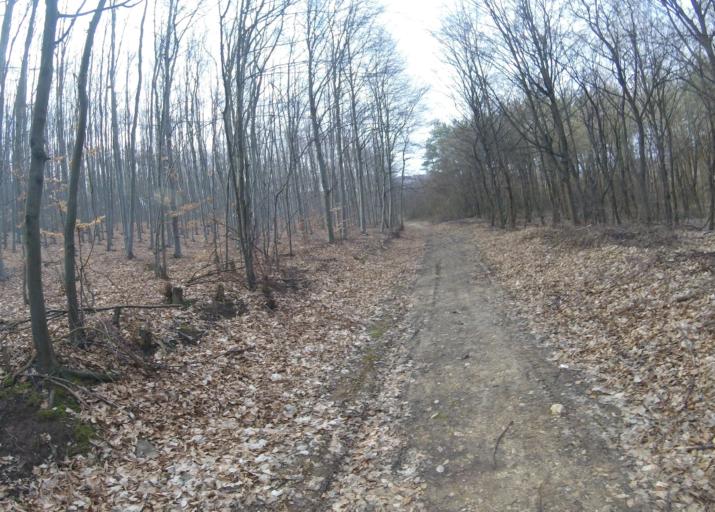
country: HU
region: Heves
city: Belapatfalva
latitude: 48.0445
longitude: 20.3615
